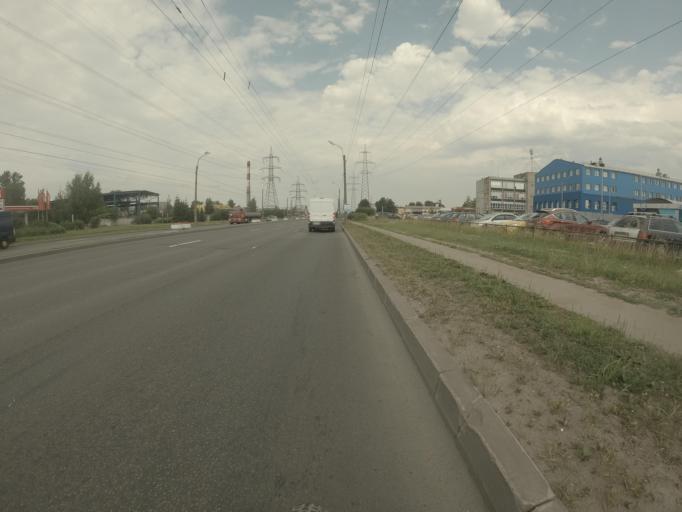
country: RU
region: St.-Petersburg
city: Krasnogvargeisky
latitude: 59.9600
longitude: 30.4629
